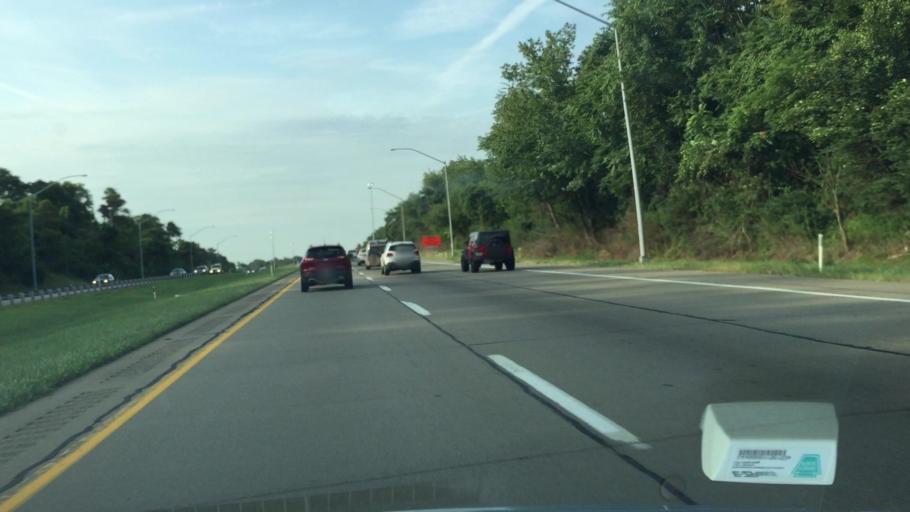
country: US
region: Pennsylvania
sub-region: Allegheny County
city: Ingram
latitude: 40.4568
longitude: -80.1117
